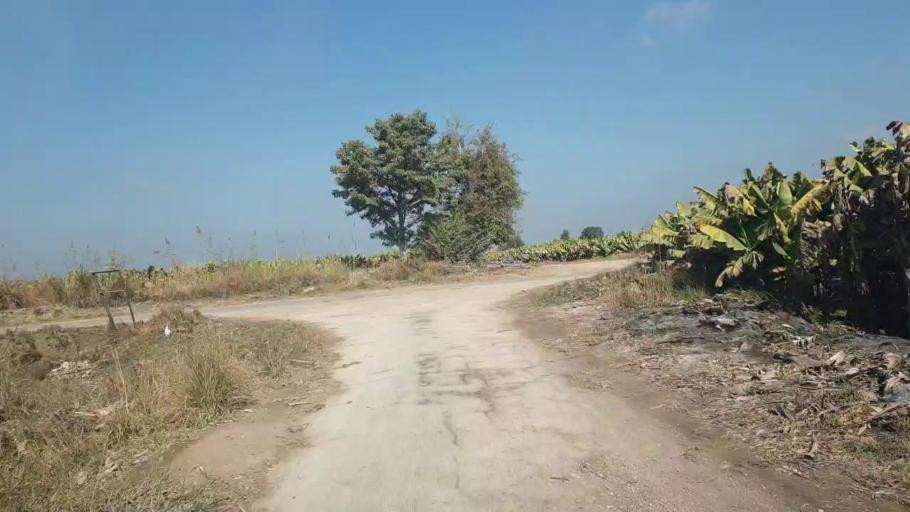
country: PK
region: Sindh
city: Shahdadpur
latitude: 25.9195
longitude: 68.5863
